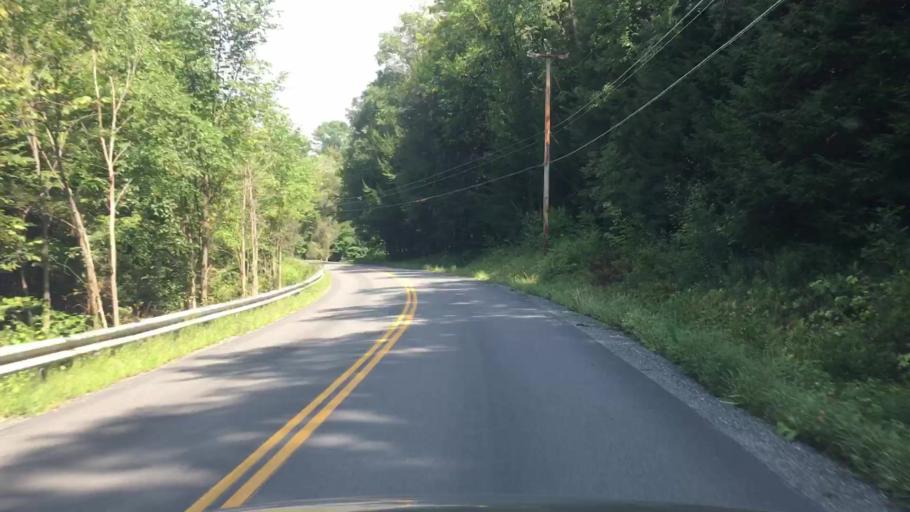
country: US
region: Vermont
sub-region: Windham County
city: West Brattleboro
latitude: 42.8037
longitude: -72.6187
